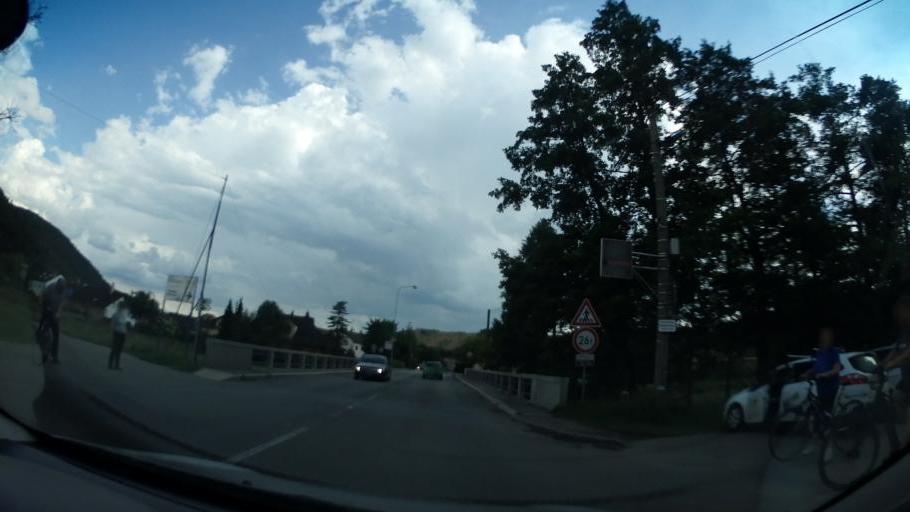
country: CZ
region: South Moravian
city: Predklasteri
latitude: 49.3569
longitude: 16.4009
